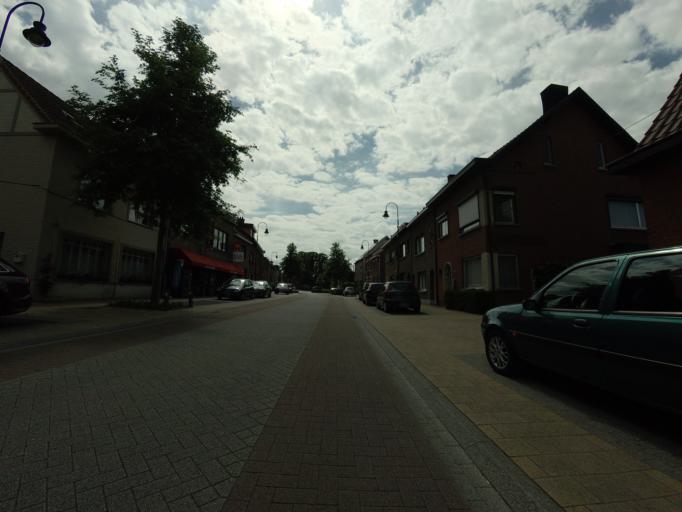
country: BE
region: Flanders
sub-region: Provincie Antwerpen
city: Lint
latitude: 51.1290
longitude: 4.4744
